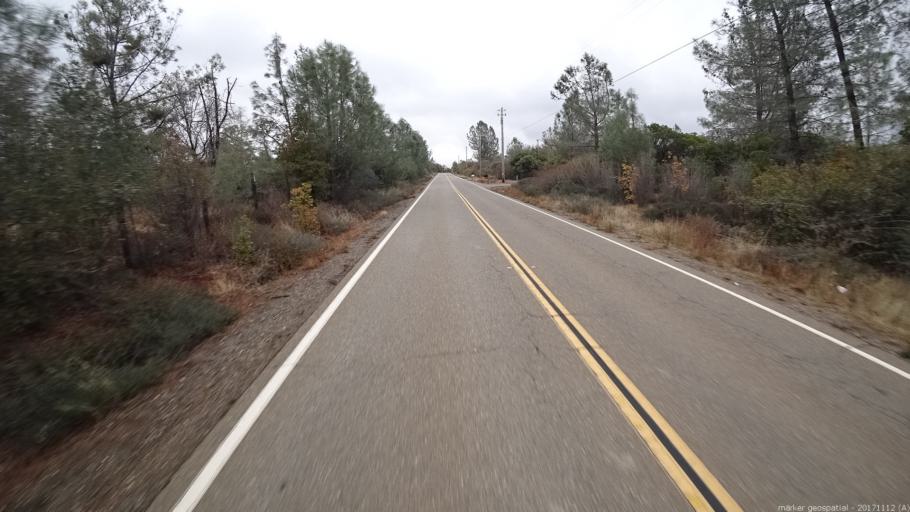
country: US
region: California
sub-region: Shasta County
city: Shingletown
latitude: 40.5109
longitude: -122.0342
